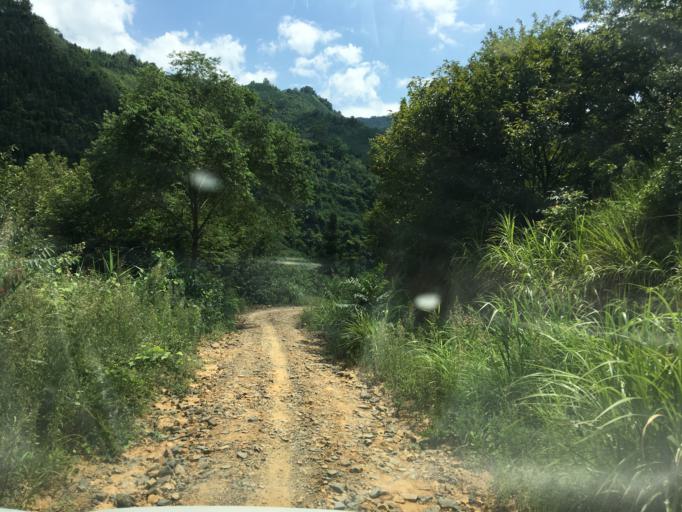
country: CN
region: Guangxi Zhuangzu Zizhiqu
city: Tongle
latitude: 24.9708
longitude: 105.9828
